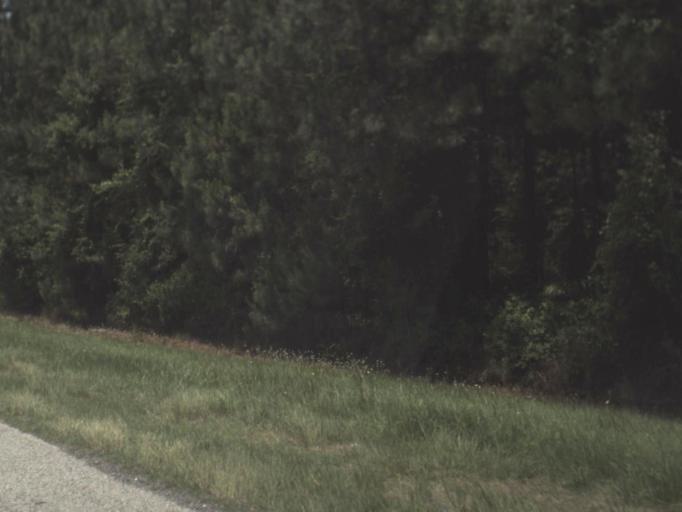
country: US
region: Florida
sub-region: Duval County
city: Baldwin
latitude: 30.2797
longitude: -81.9848
